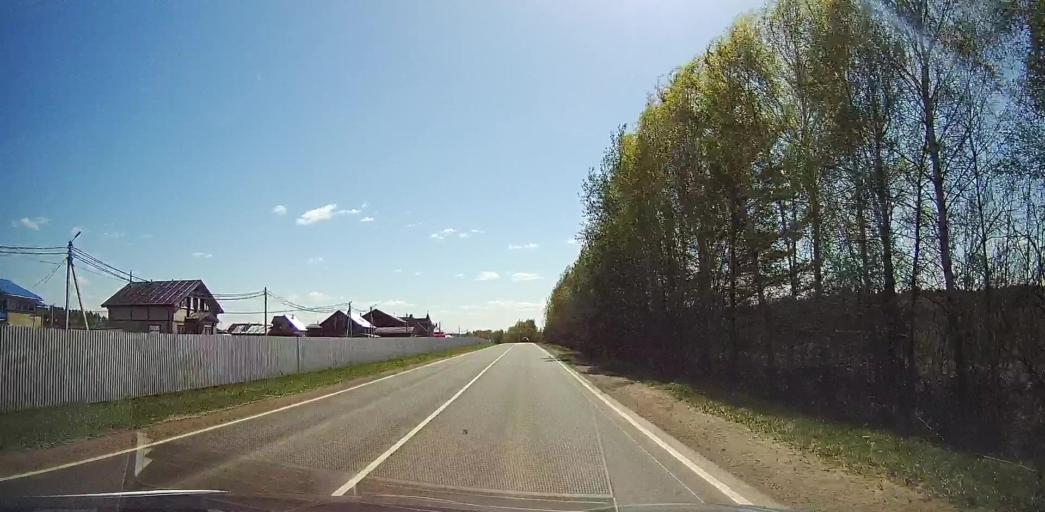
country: RU
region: Moskovskaya
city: Beloozerskiy
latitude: 55.5335
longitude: 38.4283
